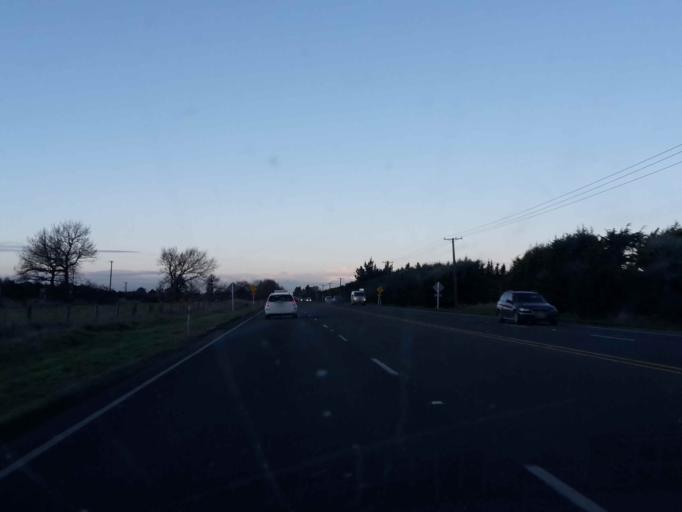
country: NZ
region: Canterbury
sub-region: Selwyn District
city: Prebbleton
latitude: -43.5588
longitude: 172.4639
